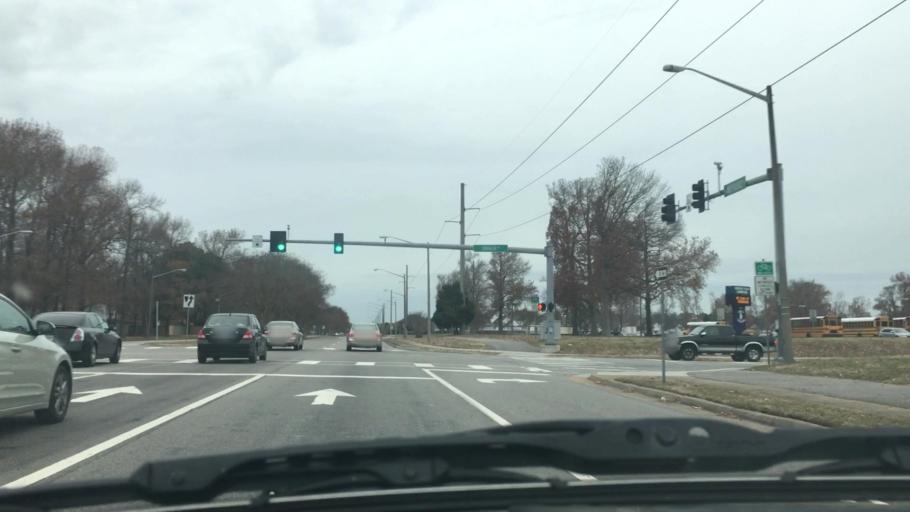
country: US
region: Virginia
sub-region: City of Virginia Beach
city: Virginia Beach
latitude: 36.8019
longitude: -76.1119
